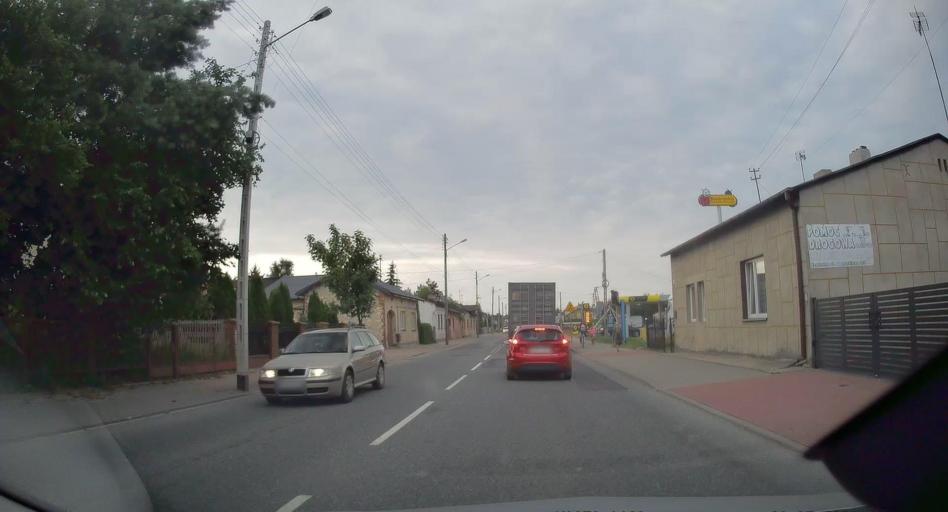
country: PL
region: Lodz Voivodeship
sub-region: Powiat radomszczanski
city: Kamiensk
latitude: 51.1944
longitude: 19.4986
